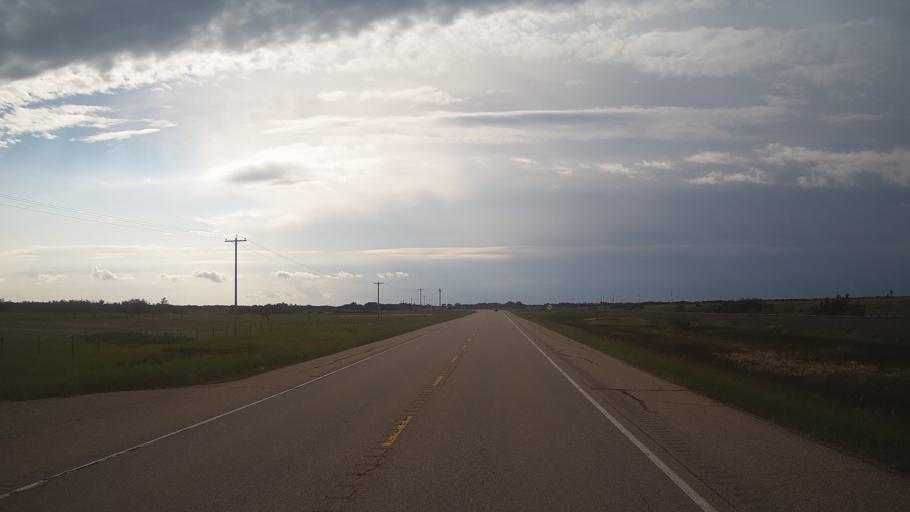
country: CA
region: Alberta
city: Viking
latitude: 53.1296
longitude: -111.9004
